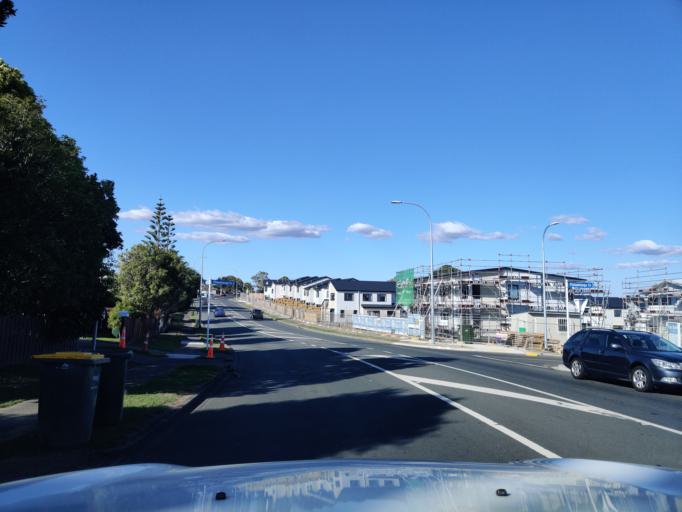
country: NZ
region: Auckland
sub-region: Auckland
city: Takanini
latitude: -37.0396
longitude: 174.8844
